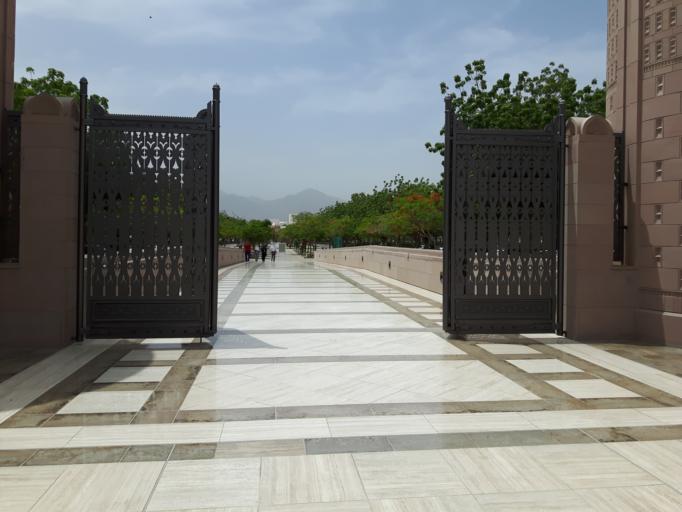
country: OM
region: Muhafazat Masqat
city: Bawshar
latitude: 23.5830
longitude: 58.3890
